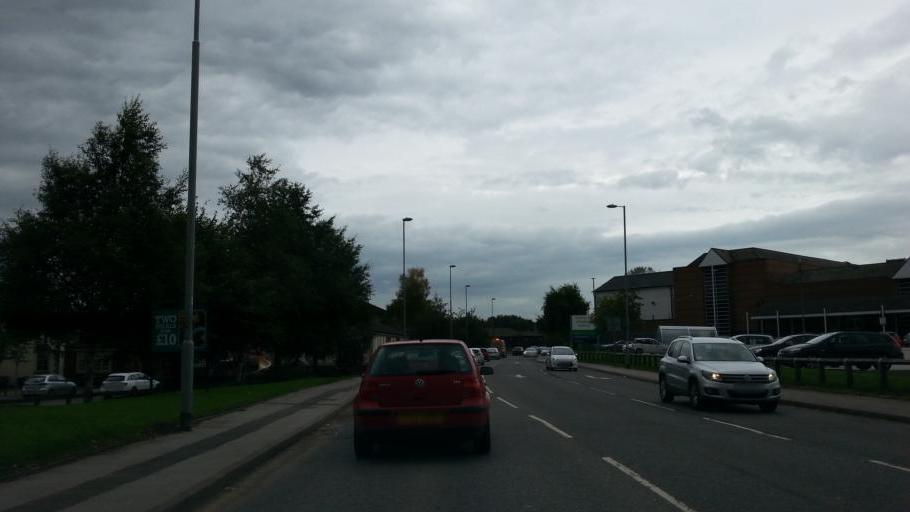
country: GB
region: England
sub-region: Borough of Bury
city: Bury
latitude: 53.5774
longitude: -2.2755
